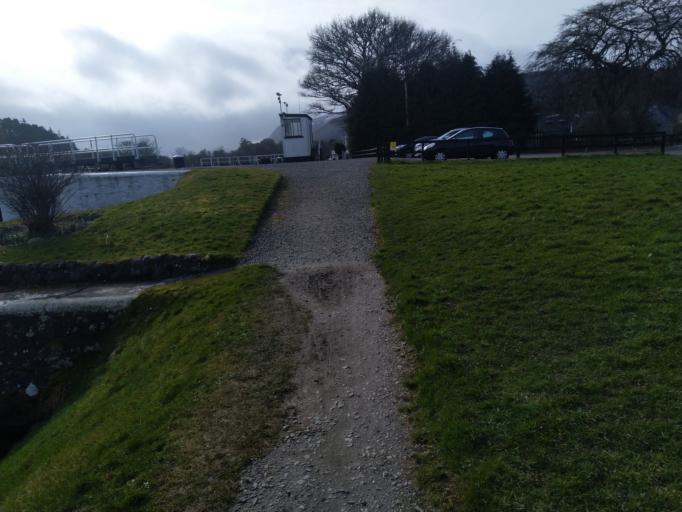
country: GB
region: Scotland
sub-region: Highland
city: Inverness
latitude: 57.4335
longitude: -4.3019
